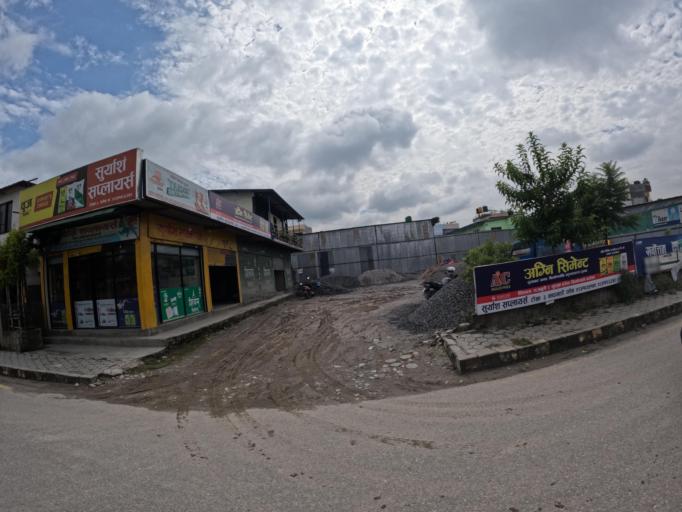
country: NP
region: Central Region
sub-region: Bagmati Zone
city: Kathmandu
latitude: 27.7586
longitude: 85.3162
